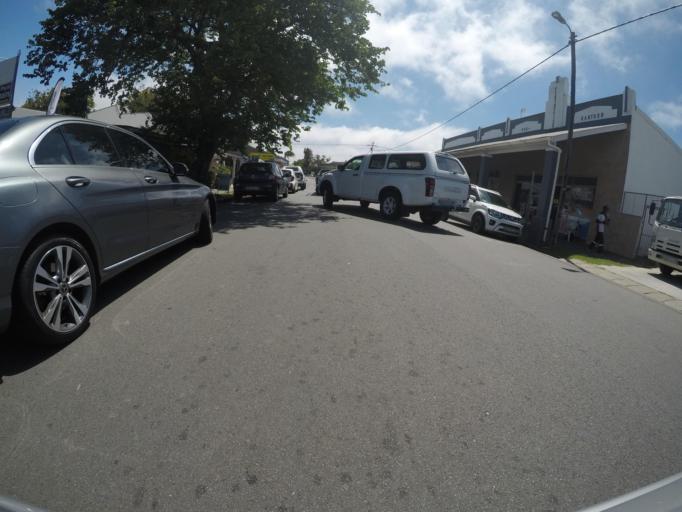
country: ZA
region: Eastern Cape
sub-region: Buffalo City Metropolitan Municipality
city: East London
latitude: -32.9788
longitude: 27.9029
